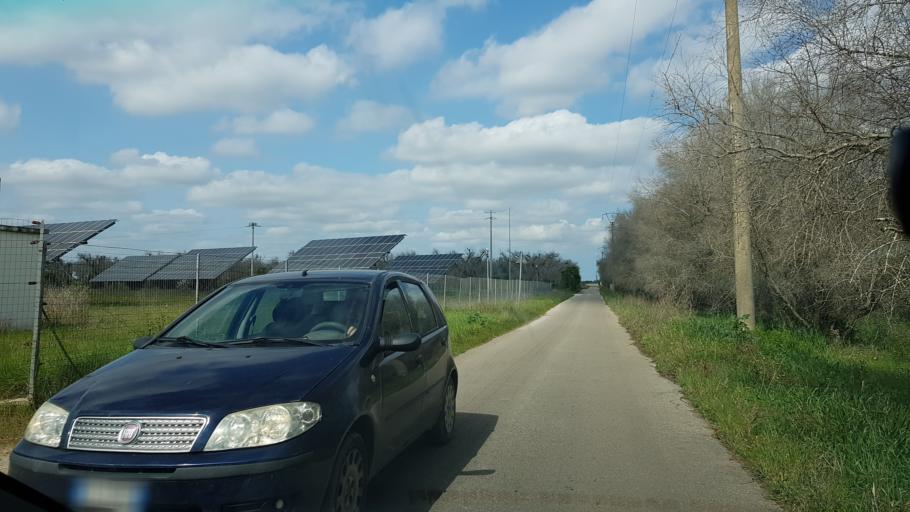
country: IT
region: Apulia
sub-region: Provincia di Brindisi
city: Torchiarolo
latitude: 40.4731
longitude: 18.0675
